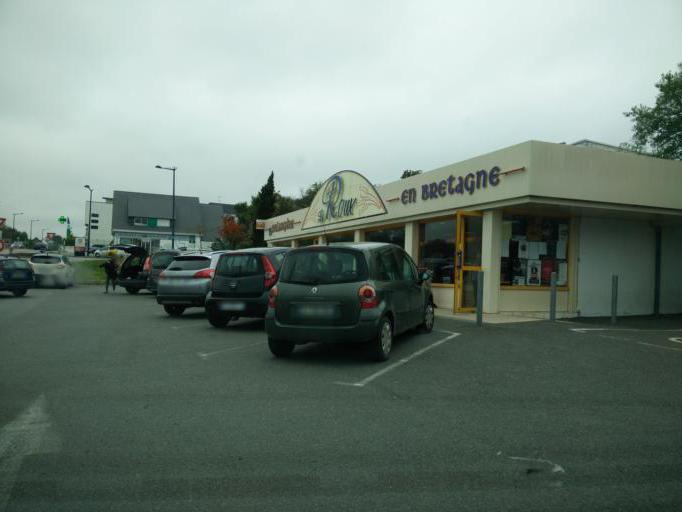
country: FR
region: Brittany
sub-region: Departement du Finistere
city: Concarneau
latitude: 47.8820
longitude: -3.9192
